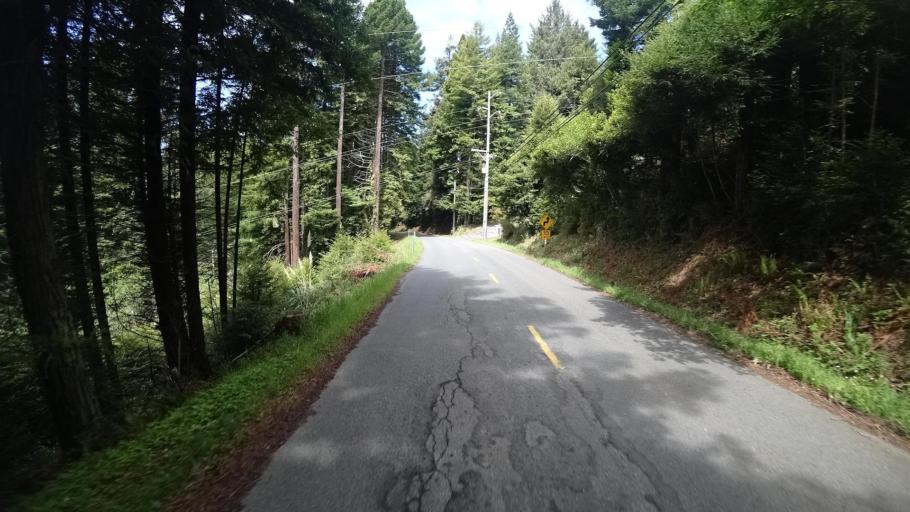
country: US
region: California
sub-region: Humboldt County
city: Arcata
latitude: 40.8689
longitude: -124.0573
